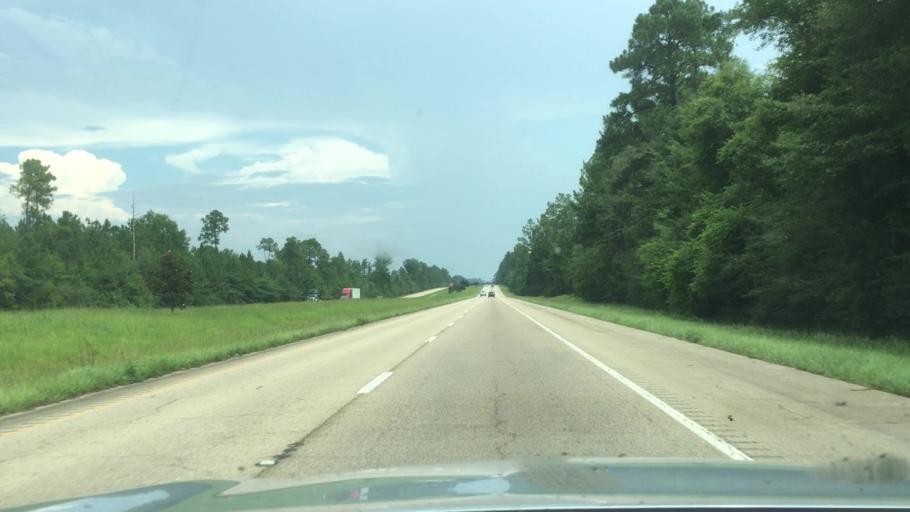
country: US
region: Mississippi
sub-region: Lamar County
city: Lumberton
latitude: 30.9683
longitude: -89.4350
